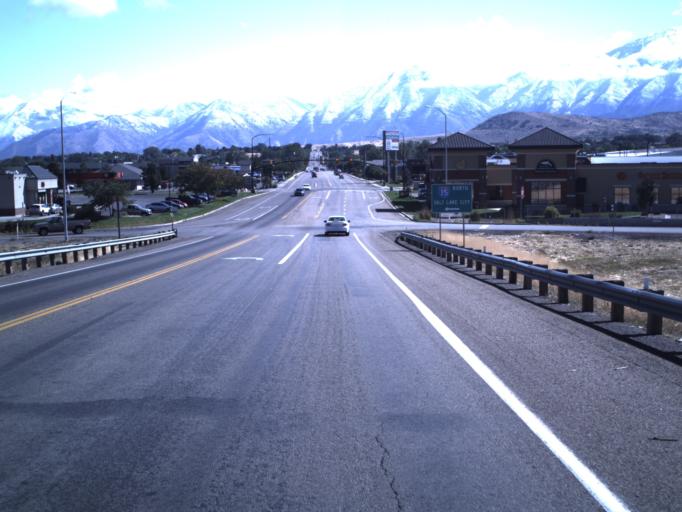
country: US
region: Utah
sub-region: Utah County
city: Payson
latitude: 40.0314
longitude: -111.7566
